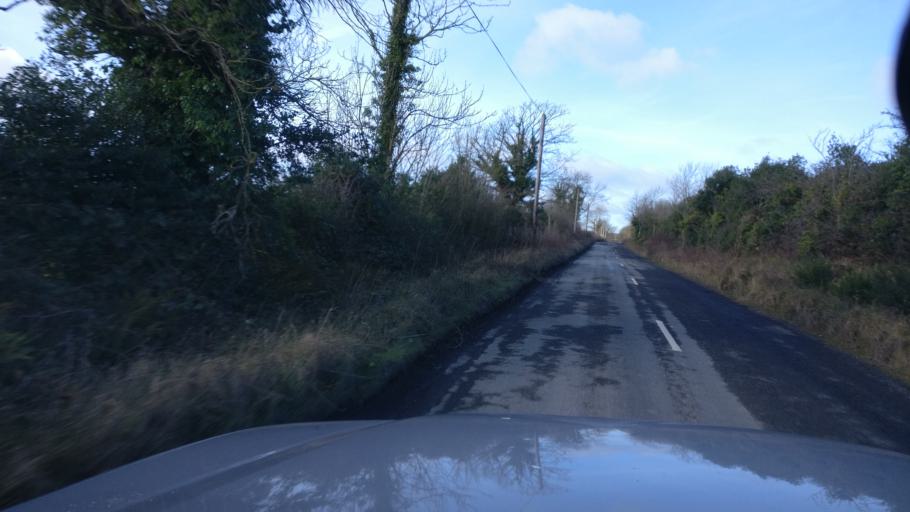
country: IE
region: Leinster
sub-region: Kilkenny
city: Castlecomer
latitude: 52.8951
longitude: -7.1705
